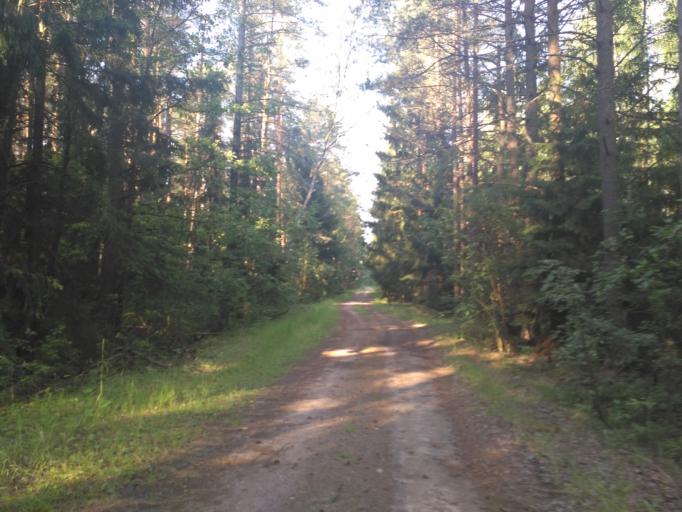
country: BY
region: Minsk
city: Chervyen'
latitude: 53.8779
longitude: 28.4588
